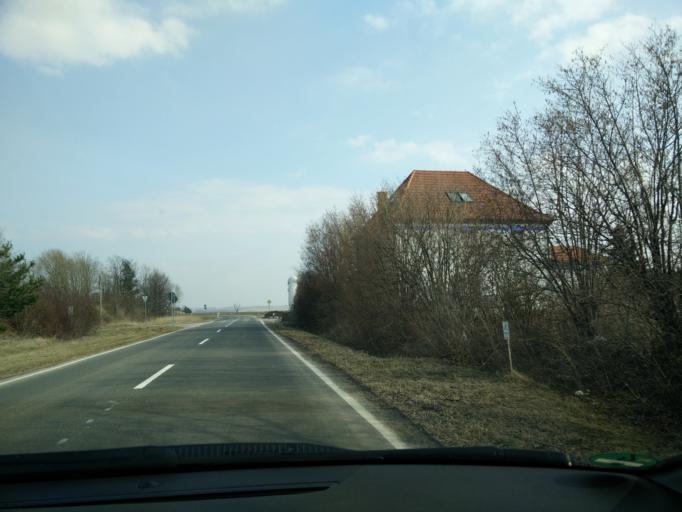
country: DE
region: Saxony
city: Konigsfeld
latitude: 51.0997
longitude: 12.7474
